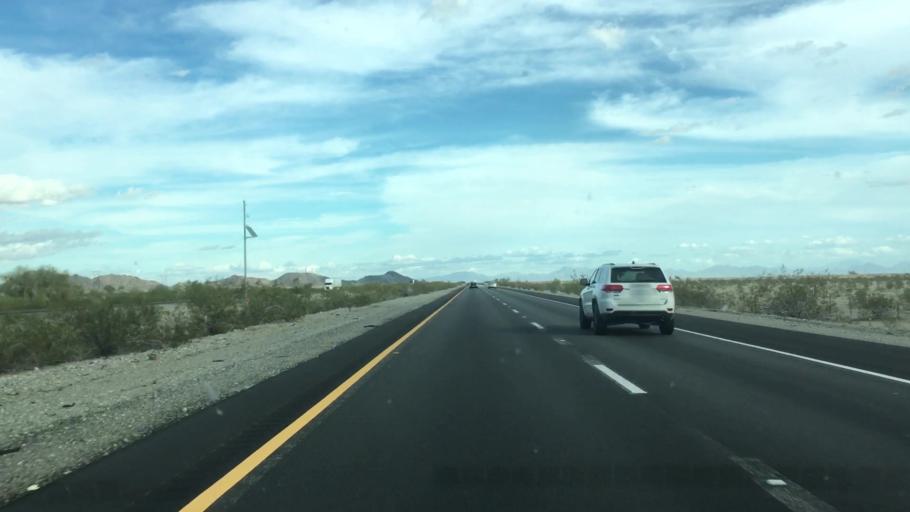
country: US
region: California
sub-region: Riverside County
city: Mesa Verde
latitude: 33.6097
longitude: -114.8253
